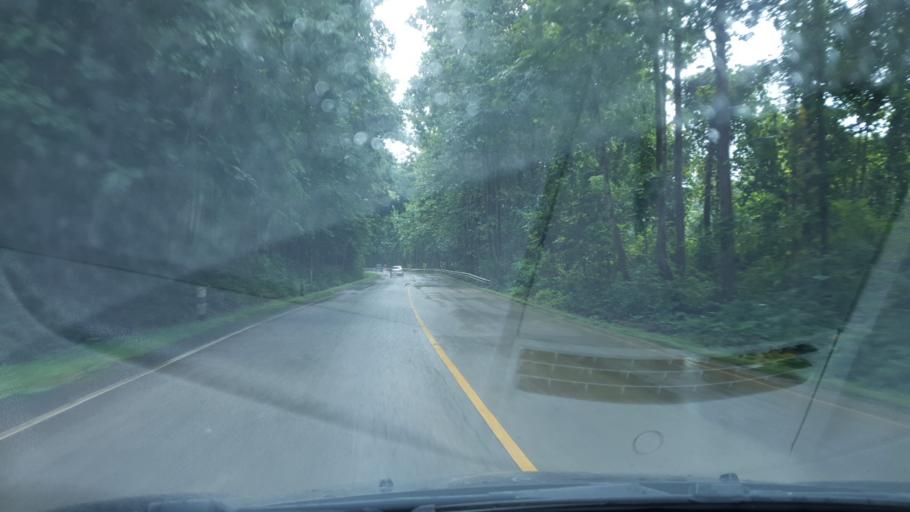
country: TH
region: Mae Hong Son
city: Pa Pae
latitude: 18.2475
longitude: 97.9429
